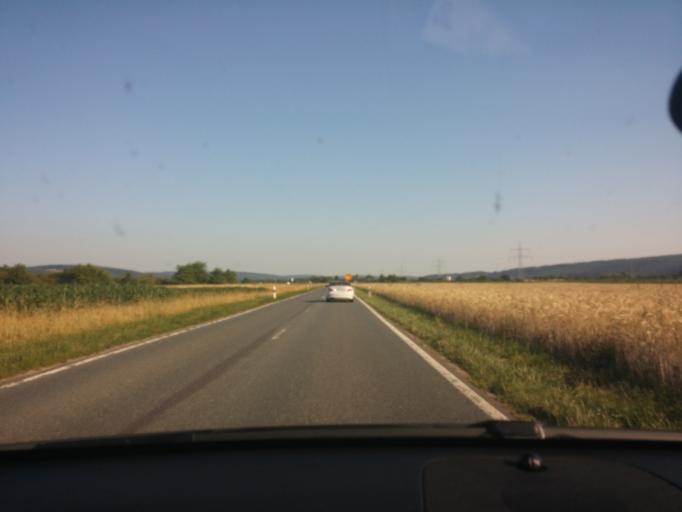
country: DE
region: Bavaria
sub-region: Regierungsbezirk Unterfranken
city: Niedernberg
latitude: 49.9082
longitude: 9.1289
